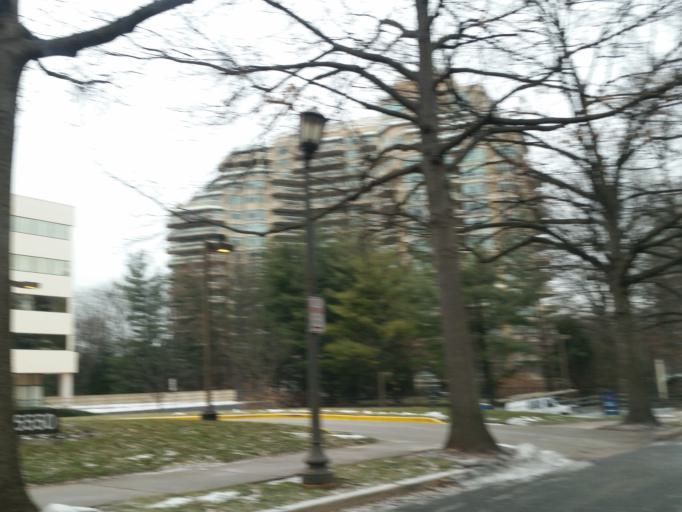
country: US
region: Maryland
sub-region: Montgomery County
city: Friendship Village
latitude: 38.9641
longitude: -77.0895
